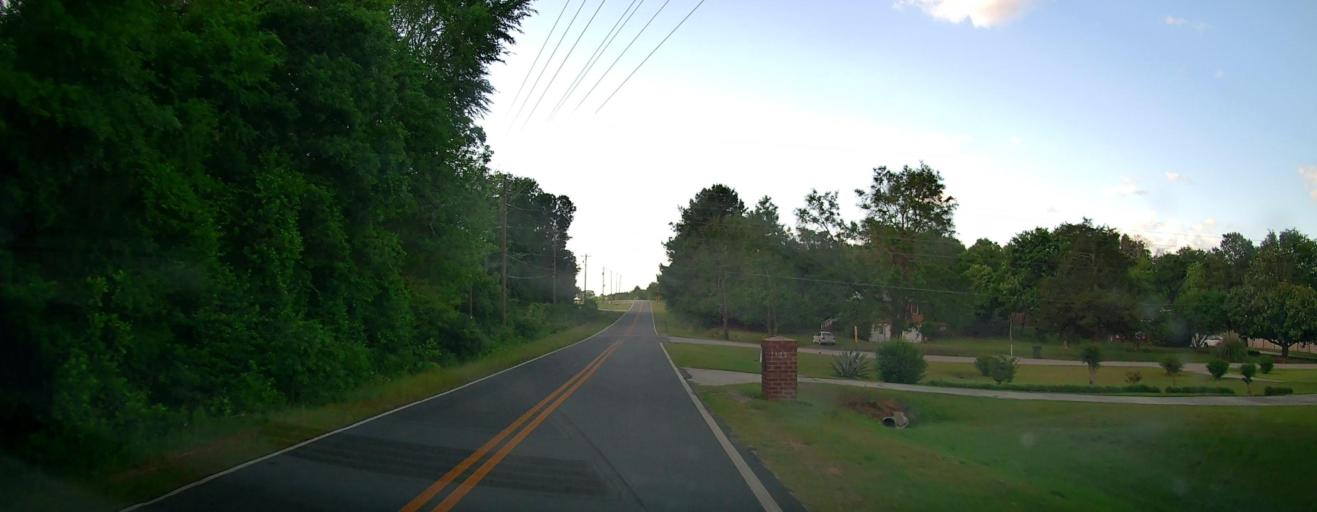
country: US
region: Georgia
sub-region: Peach County
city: Byron
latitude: 32.6348
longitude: -83.7671
